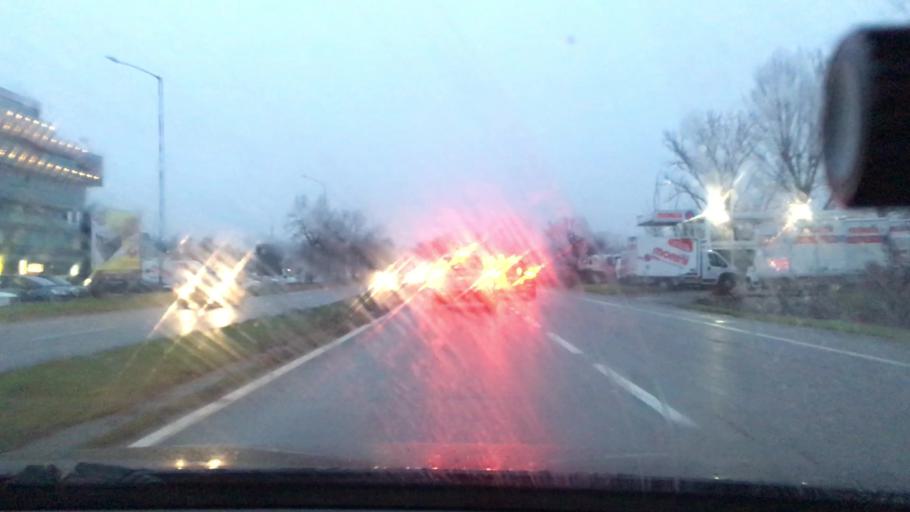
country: IT
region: Emilia-Romagna
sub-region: Provincia di Modena
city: Baggiovara
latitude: 44.6389
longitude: 10.8845
